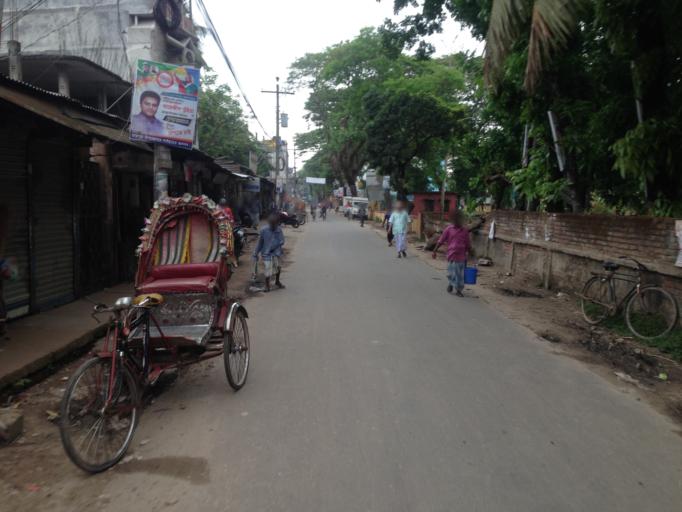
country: BD
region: Chittagong
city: Raipur
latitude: 23.0366
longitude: 90.7624
